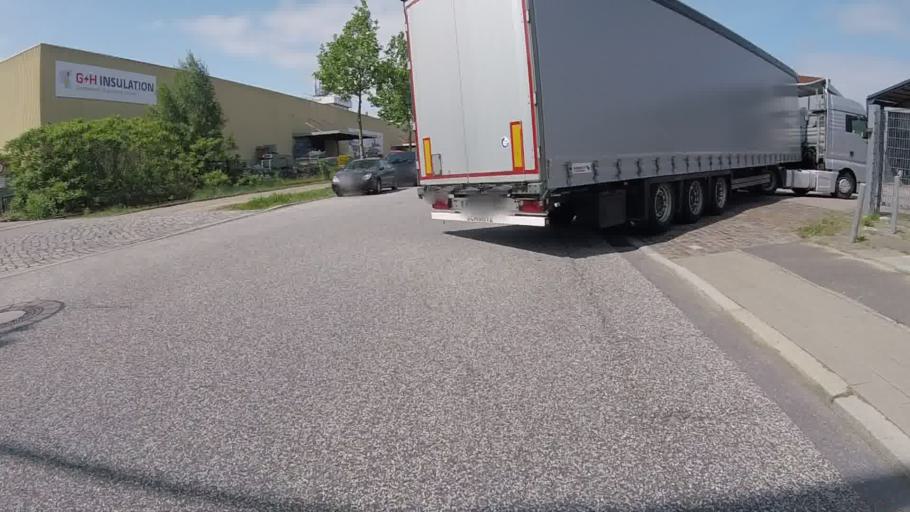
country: DE
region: Hamburg
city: Marienthal
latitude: 53.5240
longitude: 10.0848
